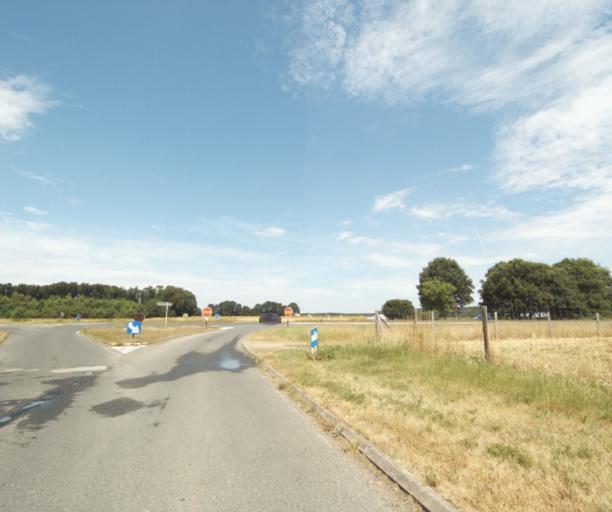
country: FR
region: Ile-de-France
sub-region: Departement de Seine-et-Marne
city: Perthes
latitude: 48.4632
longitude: 2.5551
